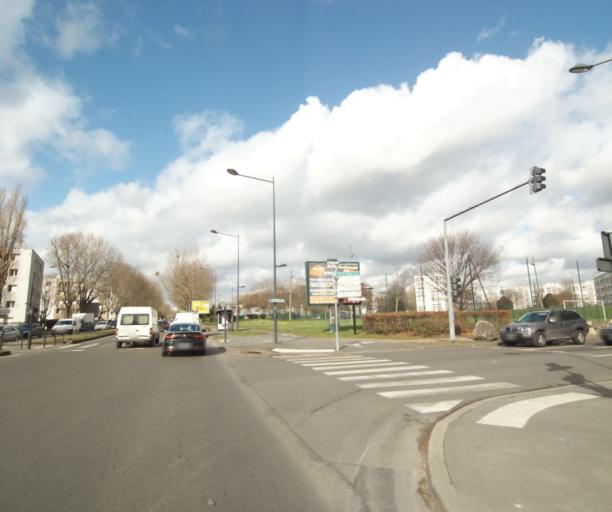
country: FR
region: Ile-de-France
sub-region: Departement de Seine-Saint-Denis
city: Saint-Denis
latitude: 48.9395
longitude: 2.3692
